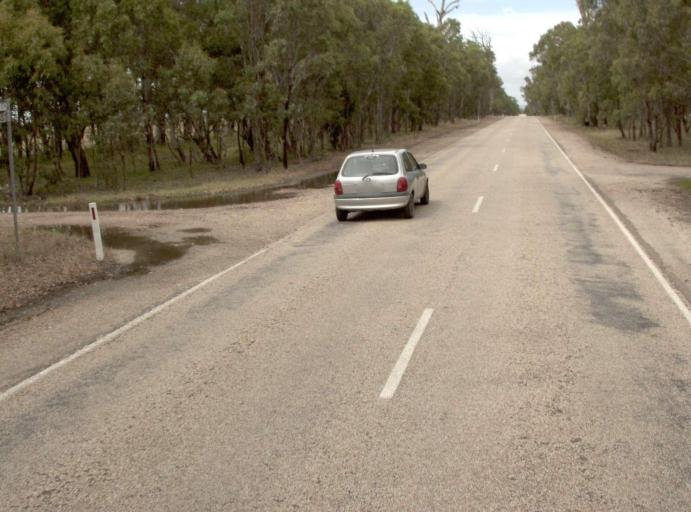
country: AU
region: Victoria
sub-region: Wellington
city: Sale
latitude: -37.9358
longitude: 147.0956
